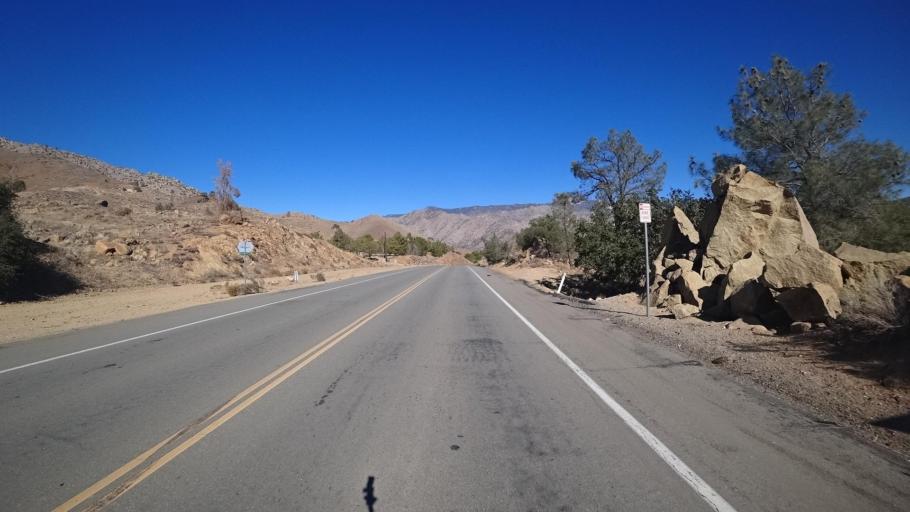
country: US
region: California
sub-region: Kern County
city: Wofford Heights
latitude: 35.7180
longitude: -118.4385
